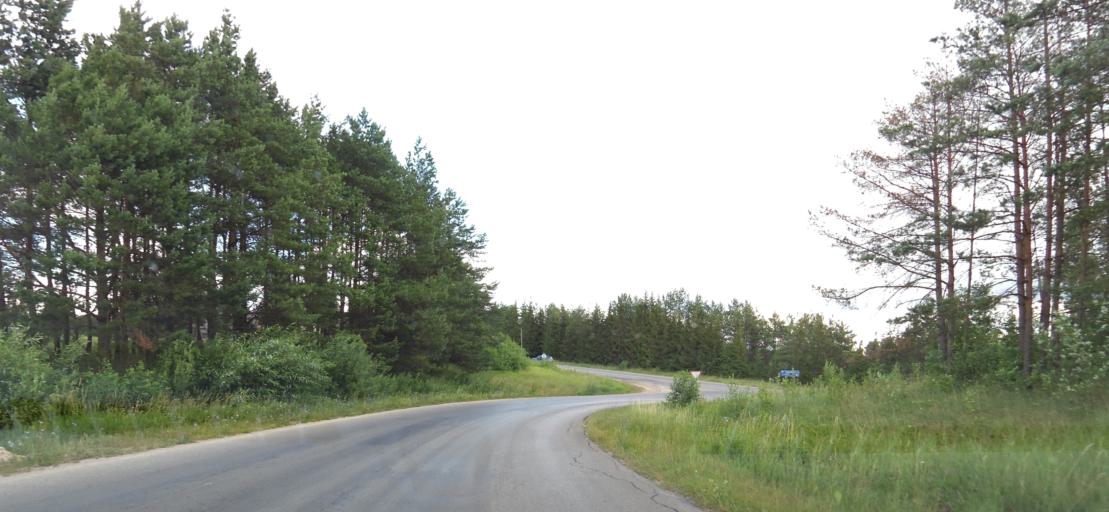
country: LT
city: Kupiskis
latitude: 55.8482
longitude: 24.9636
